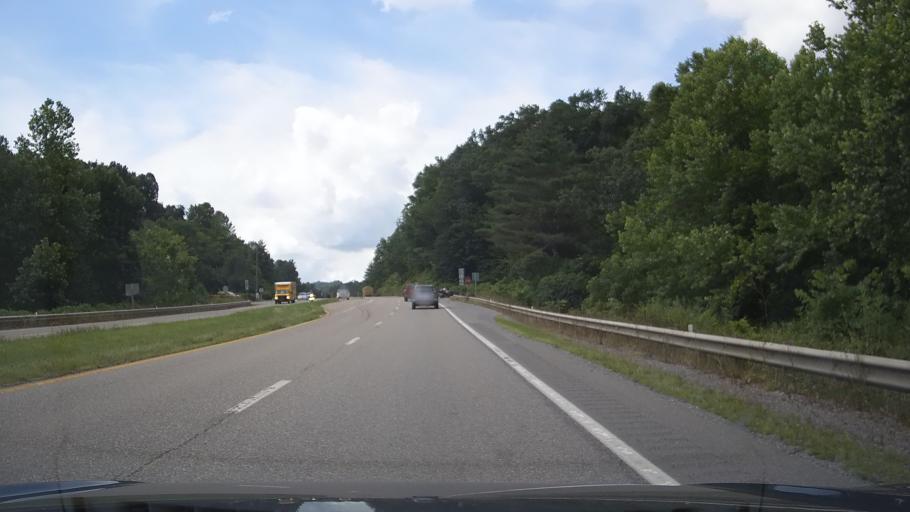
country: US
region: Virginia
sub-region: Wise County
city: Pound
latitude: 37.1265
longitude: -82.6212
